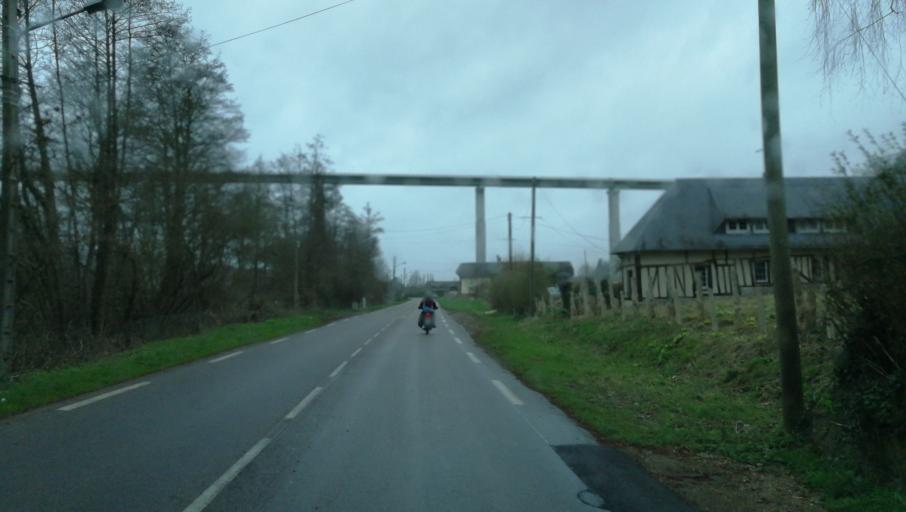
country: FR
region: Haute-Normandie
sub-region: Departement de l'Eure
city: Brionne
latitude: 49.1612
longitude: 0.7261
